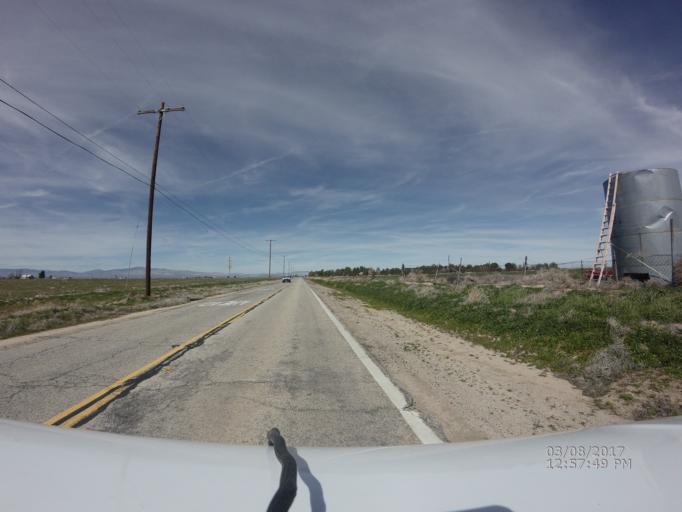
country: US
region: California
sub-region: Los Angeles County
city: Quartz Hill
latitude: 34.7048
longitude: -118.2544
